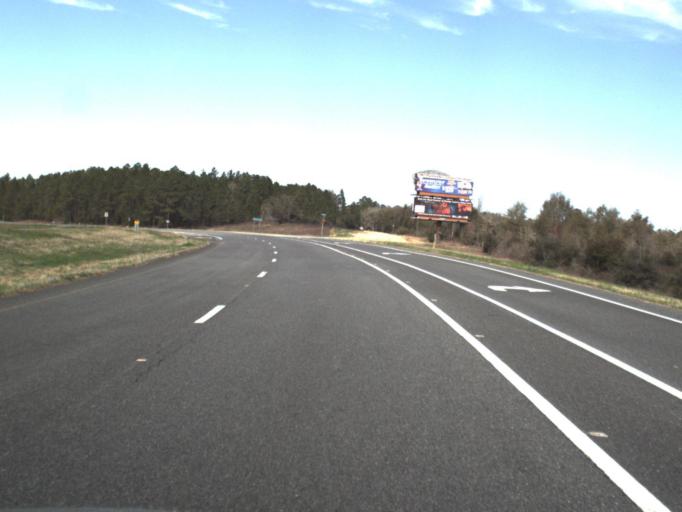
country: US
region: Florida
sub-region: Bay County
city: Youngstown
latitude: 30.5766
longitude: -85.3867
